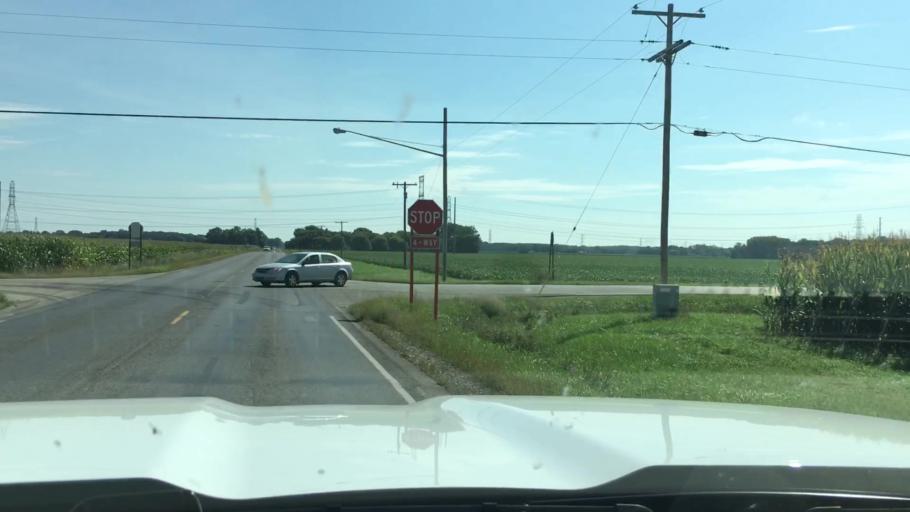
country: US
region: Michigan
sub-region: Saginaw County
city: Freeland
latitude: 43.5253
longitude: -84.1898
